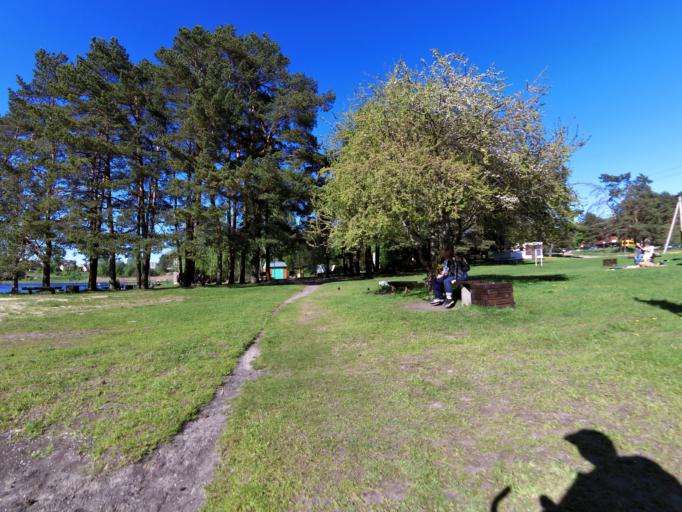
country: LT
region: Vilnius County
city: Pilaite
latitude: 54.6955
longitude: 25.1788
